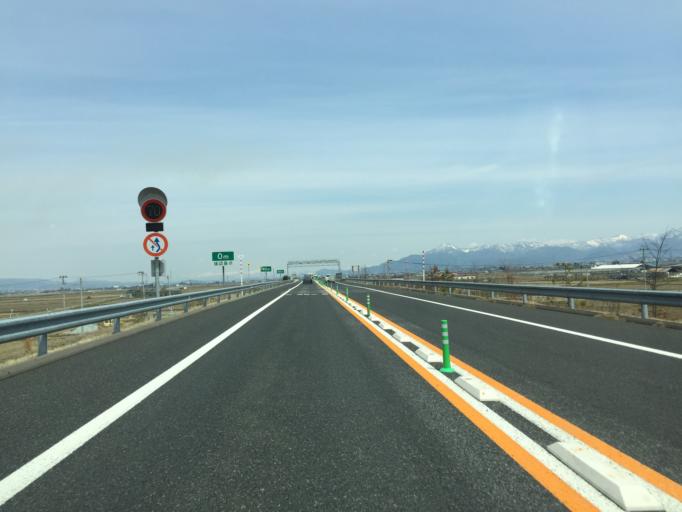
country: JP
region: Yamagata
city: Tendo
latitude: 38.3371
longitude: 140.3318
